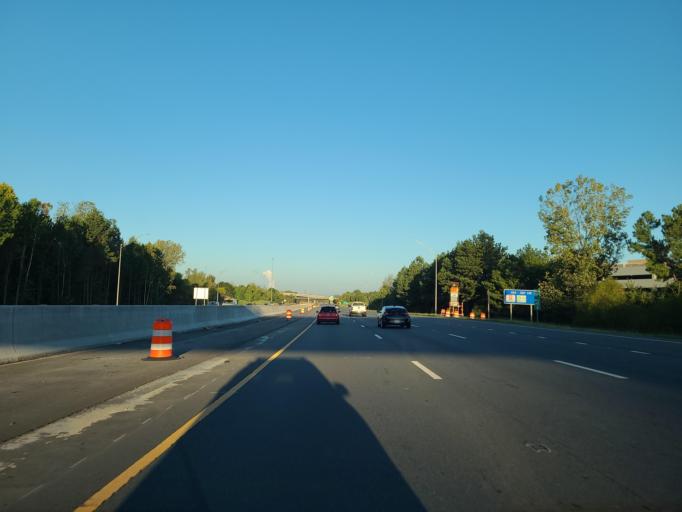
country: US
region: North Carolina
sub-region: Mecklenburg County
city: Pineville
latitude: 35.0652
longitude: -80.8383
